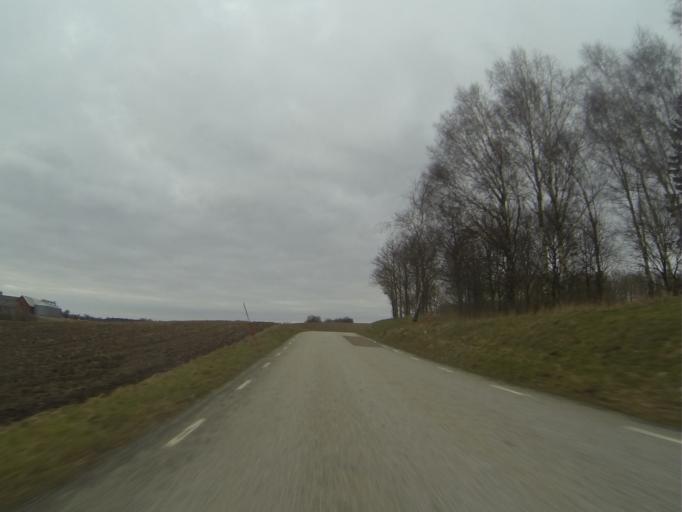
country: SE
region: Skane
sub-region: Skurups Kommun
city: Skurup
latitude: 55.5332
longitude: 13.4402
